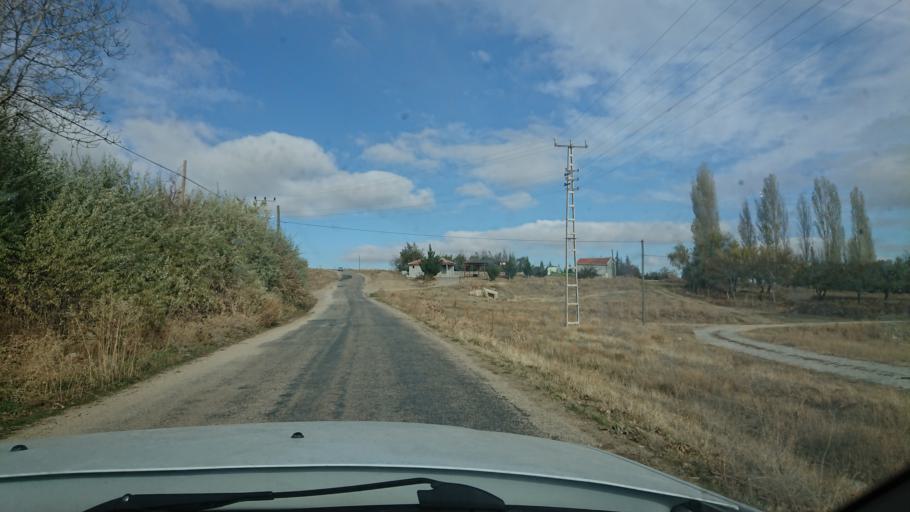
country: TR
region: Aksaray
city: Agacoren
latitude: 38.8118
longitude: 33.9837
